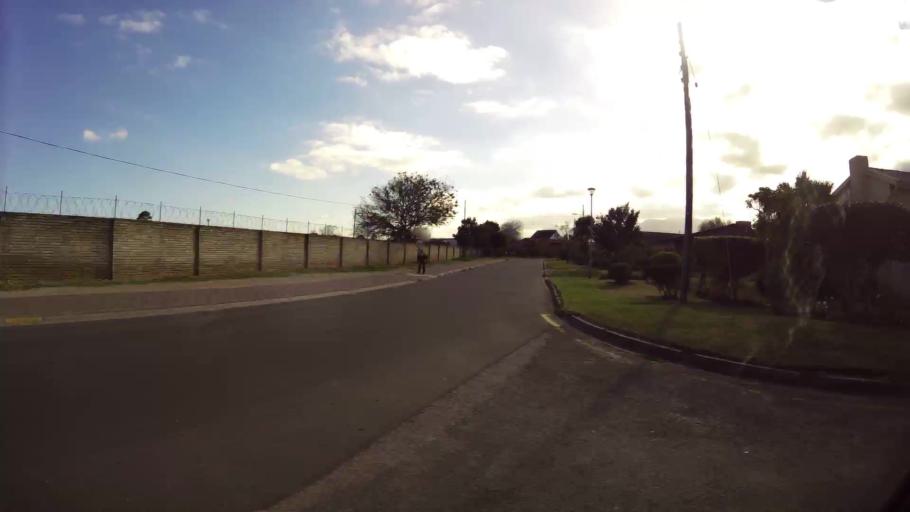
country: ZA
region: Western Cape
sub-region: Eden District Municipality
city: George
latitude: -33.9681
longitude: 22.4797
